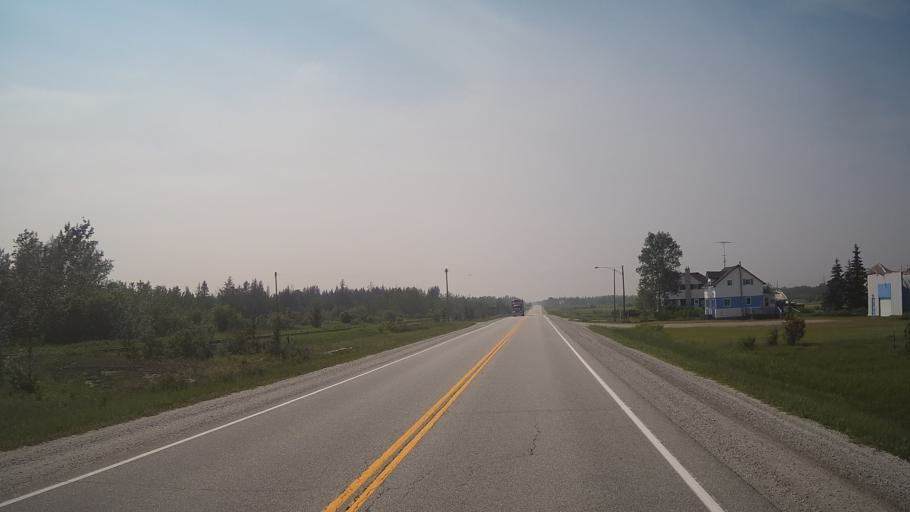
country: CA
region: Ontario
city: Kapuskasing
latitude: 49.2939
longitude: -81.9571
